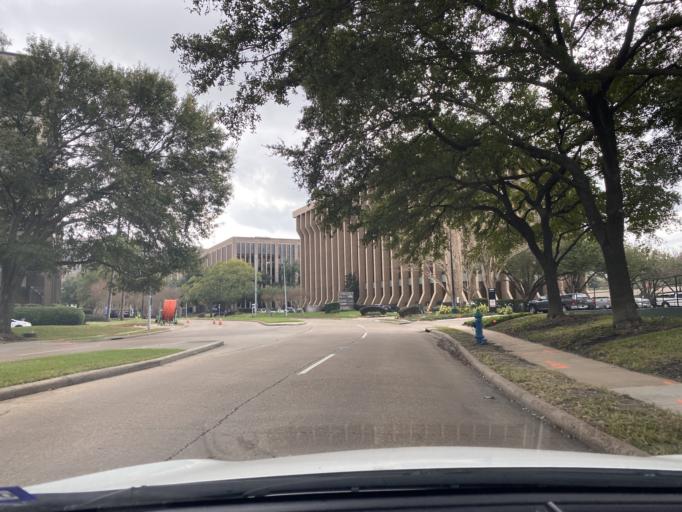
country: US
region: Texas
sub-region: Harris County
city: Hunters Creek Village
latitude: 29.7493
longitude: -95.4729
